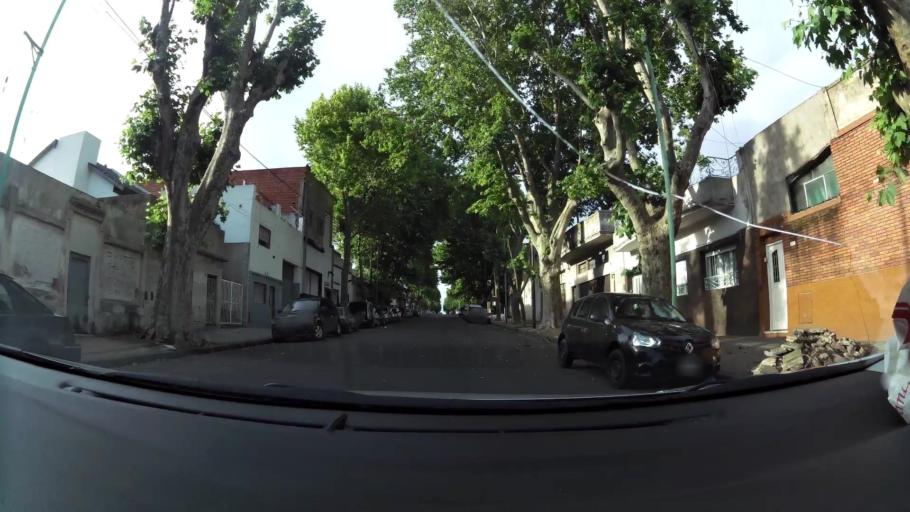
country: AR
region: Buenos Aires F.D.
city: Villa Lugano
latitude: -34.6446
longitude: -58.4277
